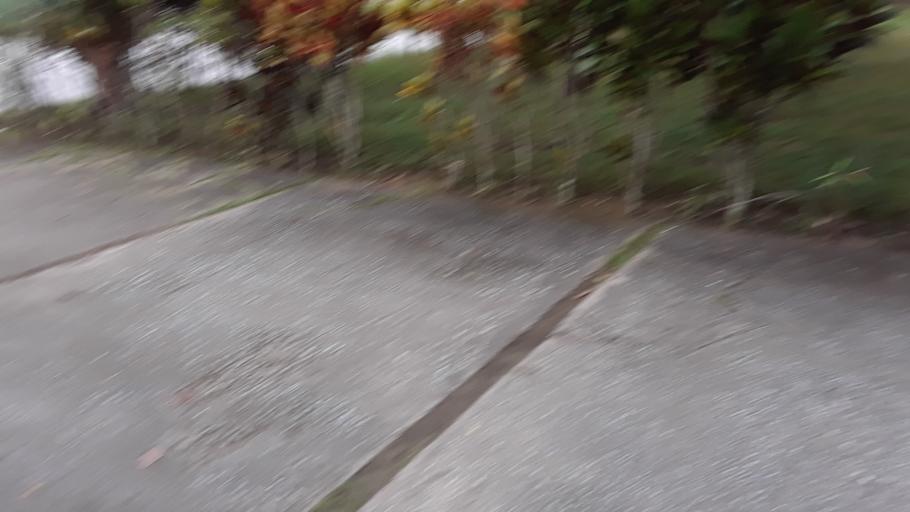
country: CU
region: Isla de la Juventud
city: Nueva Gerona
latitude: 21.8138
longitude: -82.9545
